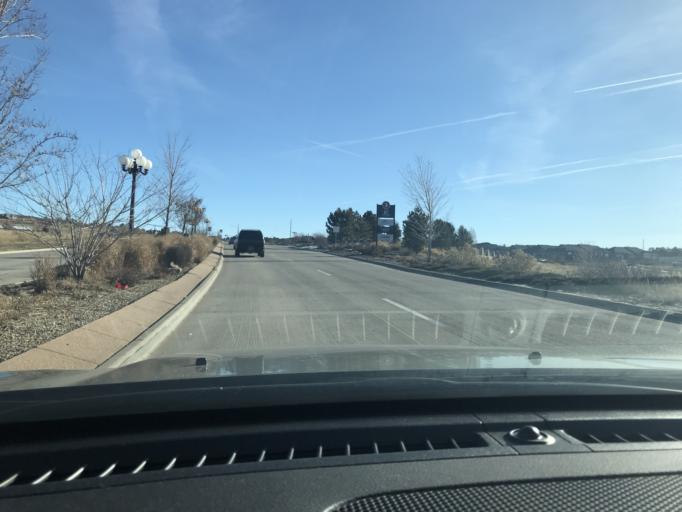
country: US
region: Colorado
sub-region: Douglas County
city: Parker
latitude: 39.5364
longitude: -104.7603
